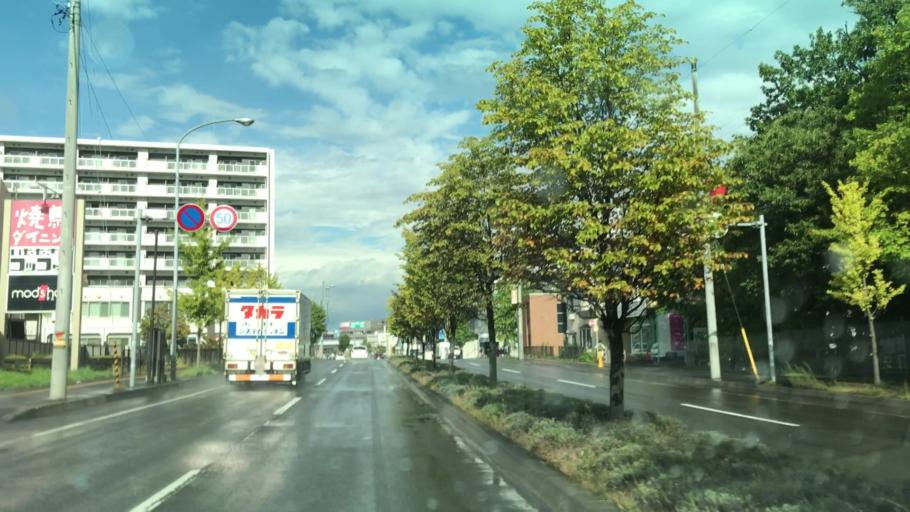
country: JP
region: Hokkaido
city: Sapporo
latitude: 43.0888
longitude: 141.2789
